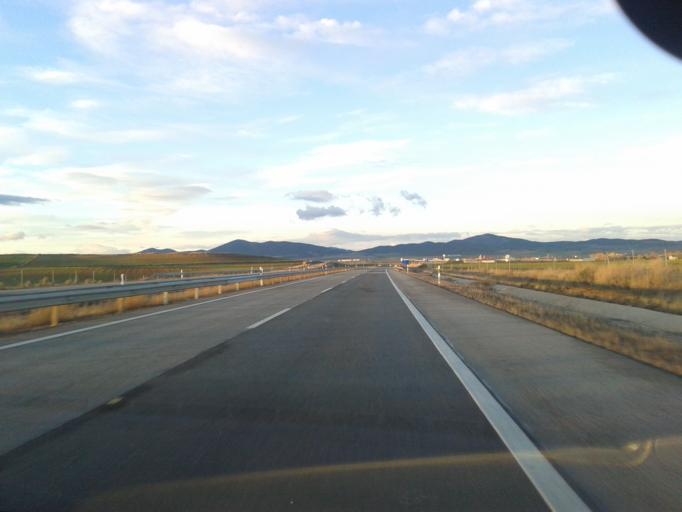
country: ES
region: Aragon
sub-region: Provincia de Zaragoza
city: Villadoz
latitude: 41.1503
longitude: -1.2927
